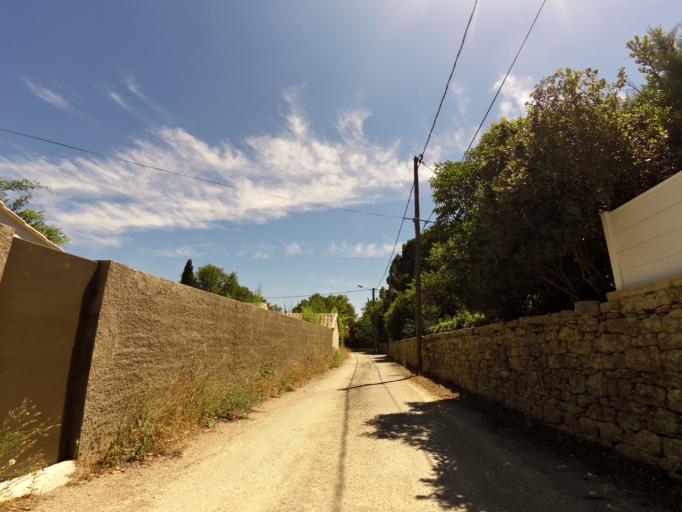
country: FR
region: Languedoc-Roussillon
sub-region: Departement du Gard
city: Aigues-Vives
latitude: 43.7436
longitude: 4.1665
